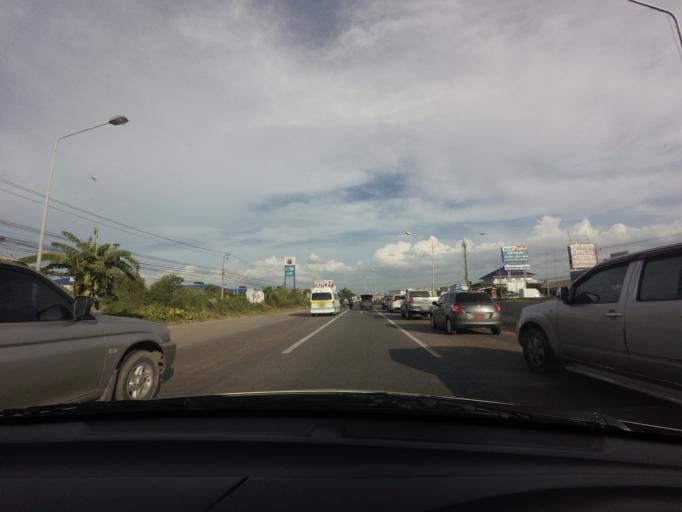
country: TH
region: Nonthaburi
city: Bang Bua Thong
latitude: 13.9714
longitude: 100.3952
